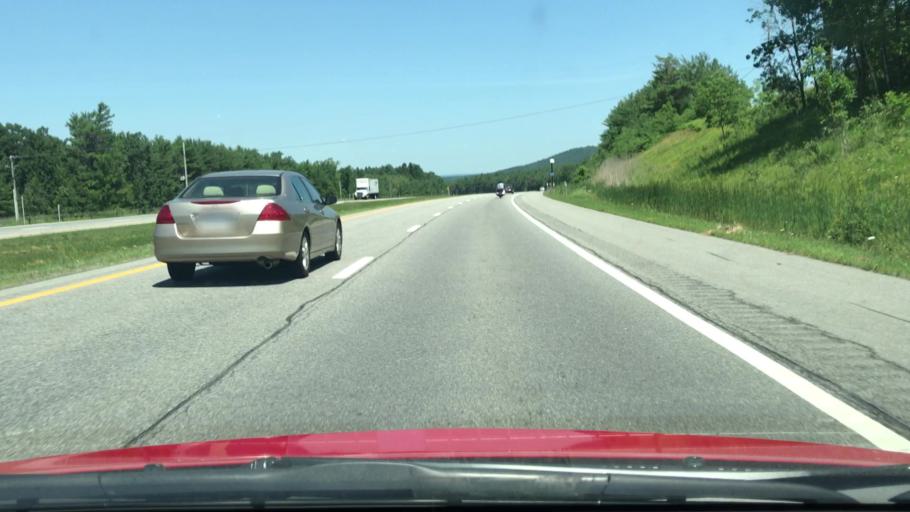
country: US
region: New York
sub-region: Essex County
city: Keeseville
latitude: 44.4539
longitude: -73.4882
